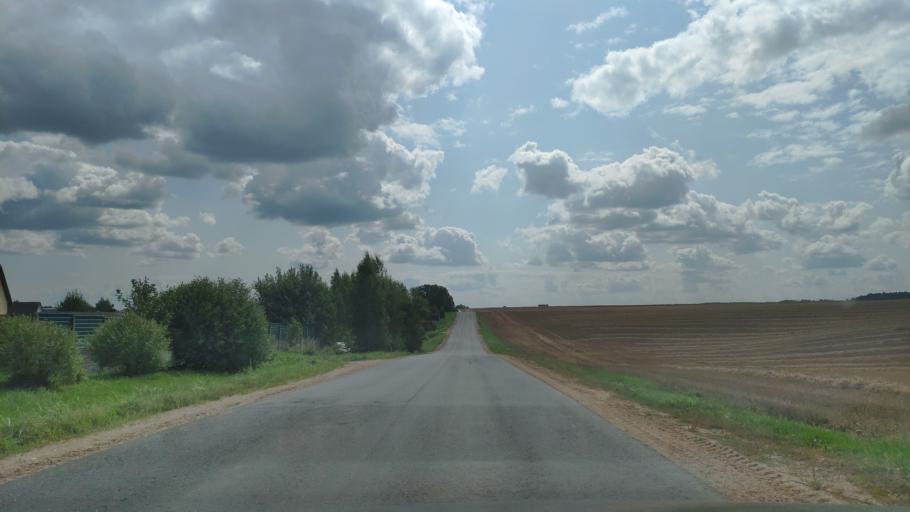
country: BY
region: Minsk
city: Khatsyezhyna
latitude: 53.8410
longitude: 27.3120
